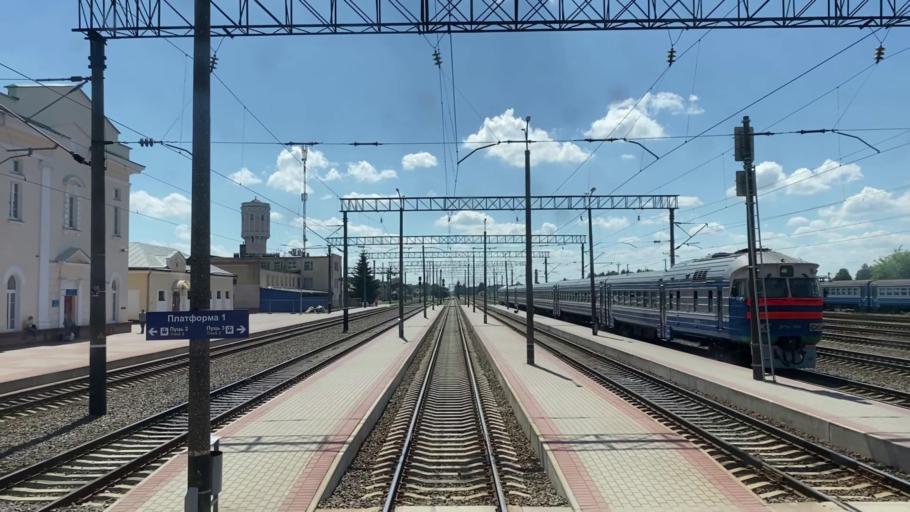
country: BY
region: Brest
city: Baranovichi
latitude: 53.1294
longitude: 26.0420
